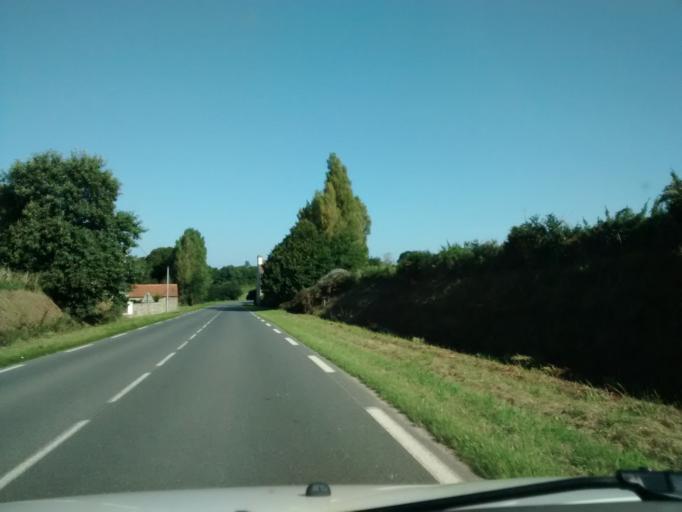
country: FR
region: Brittany
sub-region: Departement des Cotes-d'Armor
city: Tredarzec
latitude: 48.8011
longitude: -3.1998
